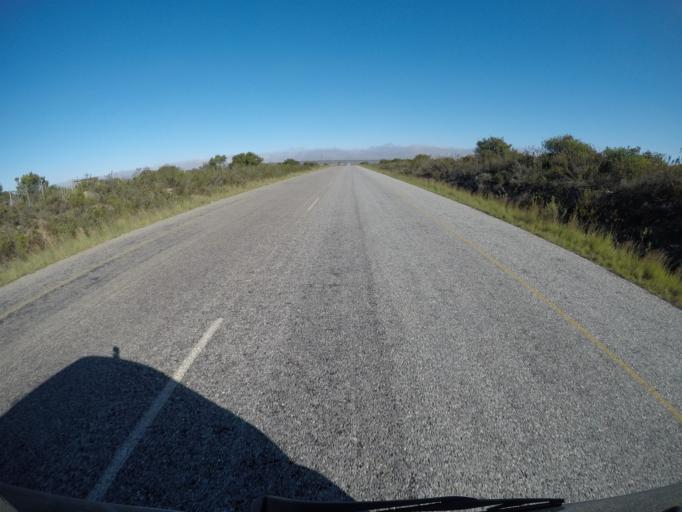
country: ZA
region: Western Cape
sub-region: Eden District Municipality
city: Mossel Bay
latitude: -34.1638
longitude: 22.0110
